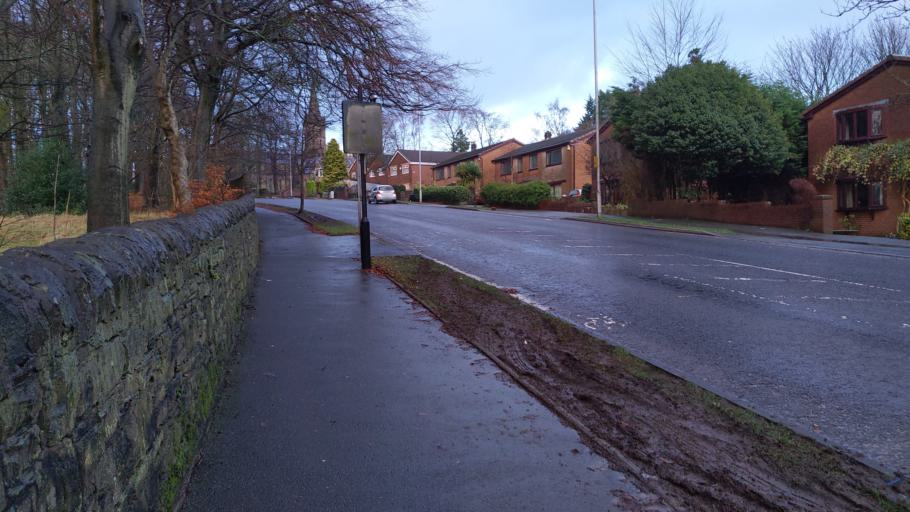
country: GB
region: England
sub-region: Blackburn with Darwen
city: Blackburn
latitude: 53.7424
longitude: -2.5085
